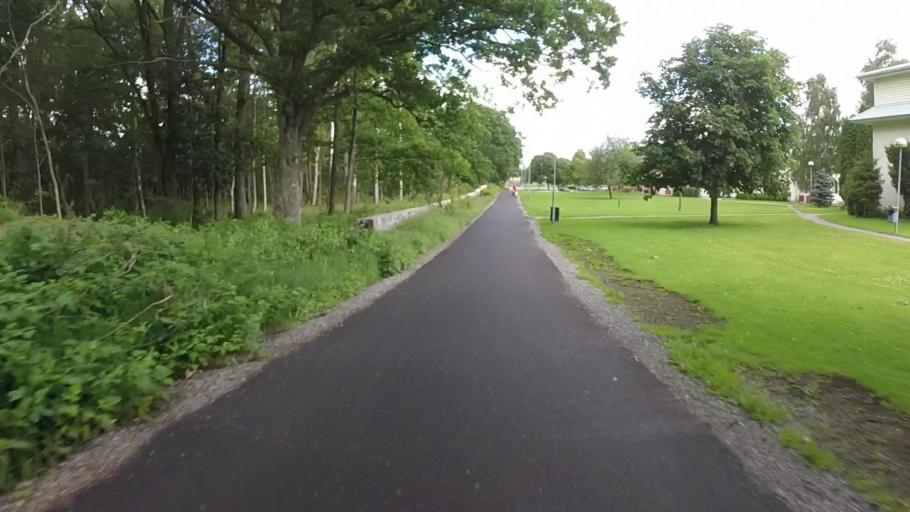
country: SE
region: Vaestra Goetaland
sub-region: Trollhattan
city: Trollhattan
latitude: 58.2732
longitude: 12.3076
